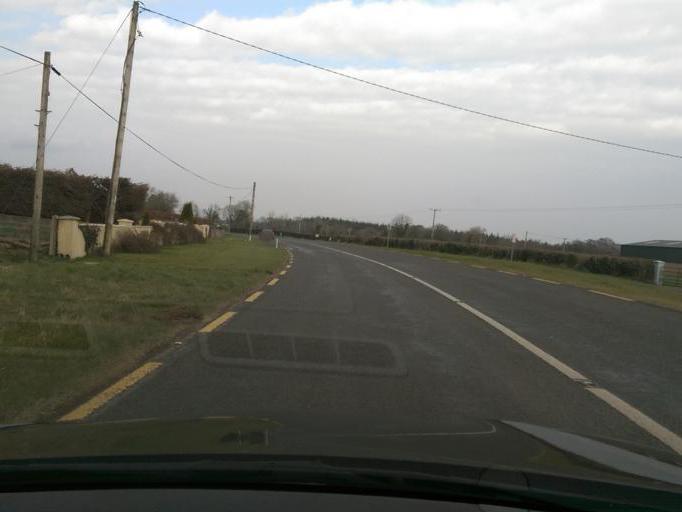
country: IE
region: Connaught
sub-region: Roscommon
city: Castlerea
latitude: 53.4964
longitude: -8.4688
